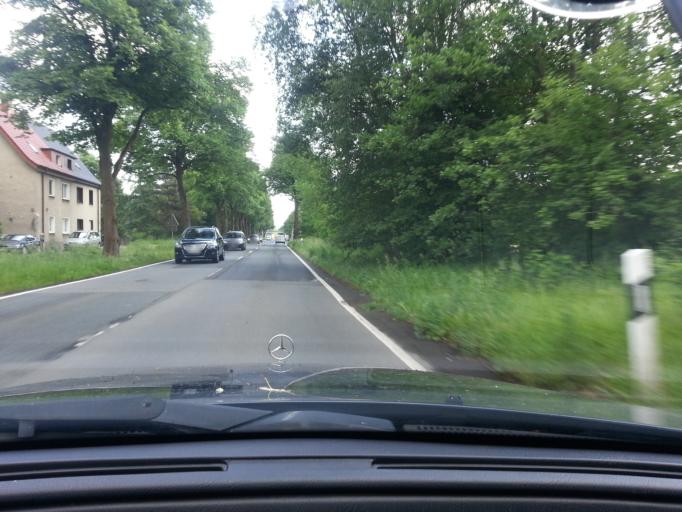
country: DE
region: North Rhine-Westphalia
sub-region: Regierungsbezirk Munster
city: Recklinghausen
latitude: 51.6574
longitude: 7.1830
